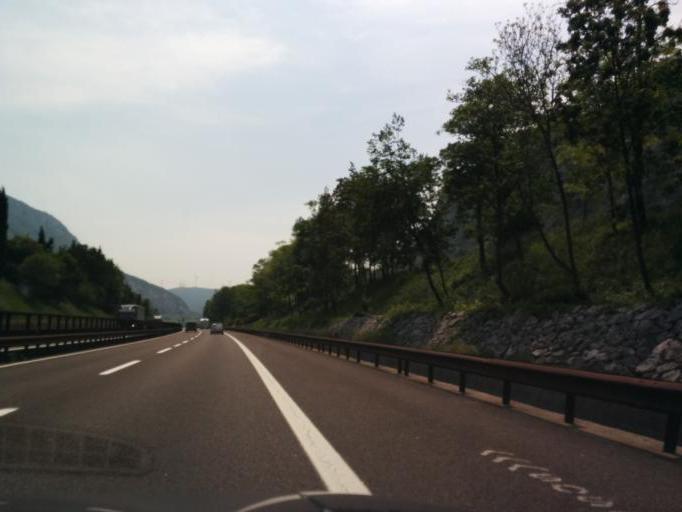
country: IT
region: Veneto
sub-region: Provincia di Verona
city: Dolce
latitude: 45.5949
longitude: 10.8388
